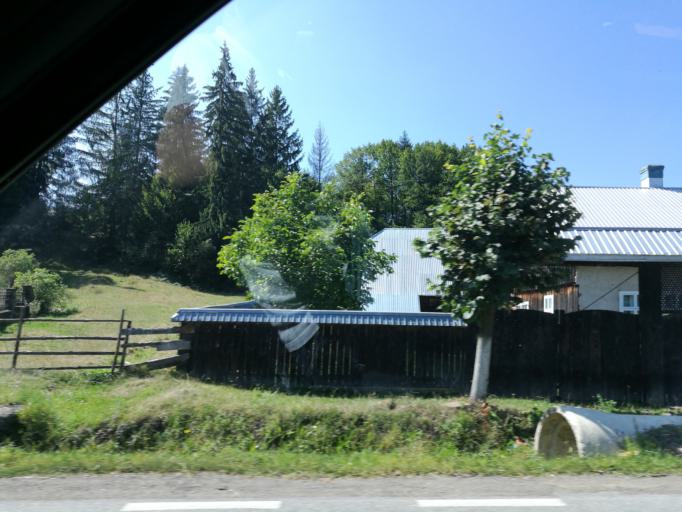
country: RO
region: Suceava
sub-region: Comuna Putna
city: Putna
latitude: 47.8842
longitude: 25.6123
